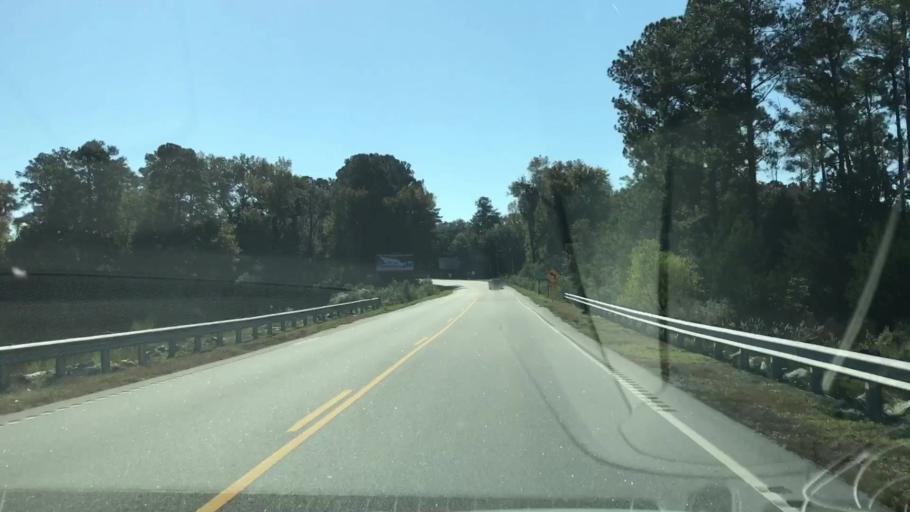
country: US
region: South Carolina
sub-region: Jasper County
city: Ridgeland
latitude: 32.5425
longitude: -80.9123
